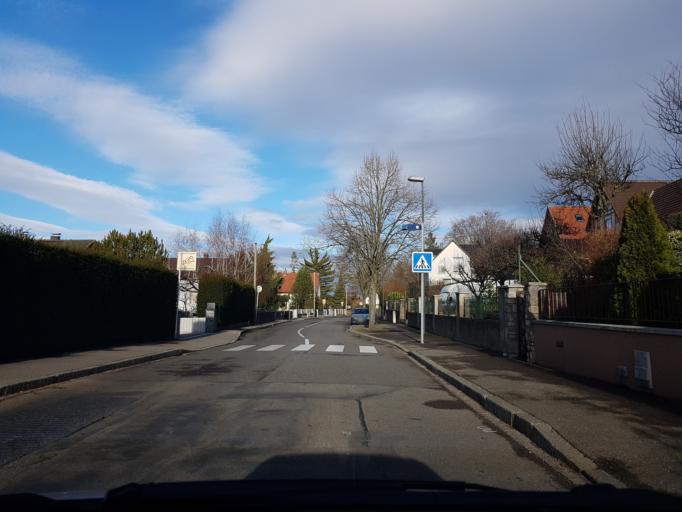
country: FR
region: Alsace
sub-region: Departement du Haut-Rhin
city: Riedisheim
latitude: 47.7514
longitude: 7.3763
